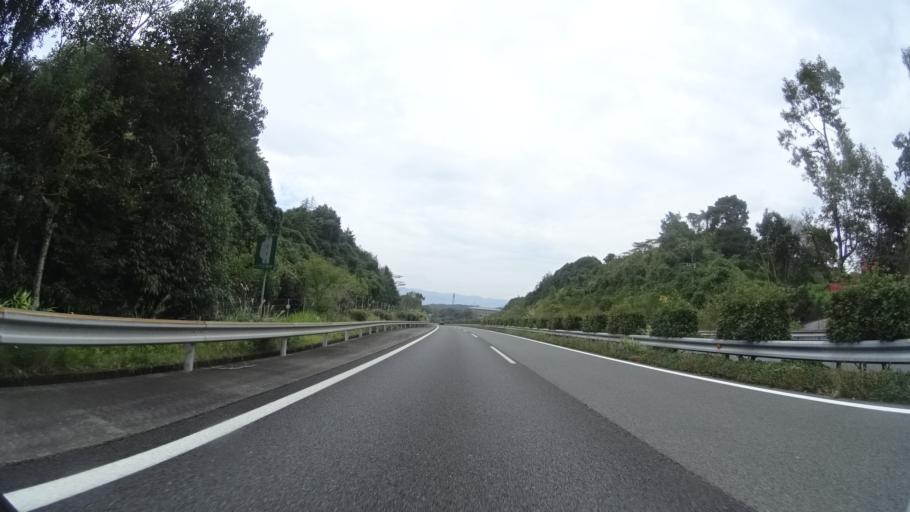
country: JP
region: Kumamoto
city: Hitoyoshi
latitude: 32.2248
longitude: 130.7788
